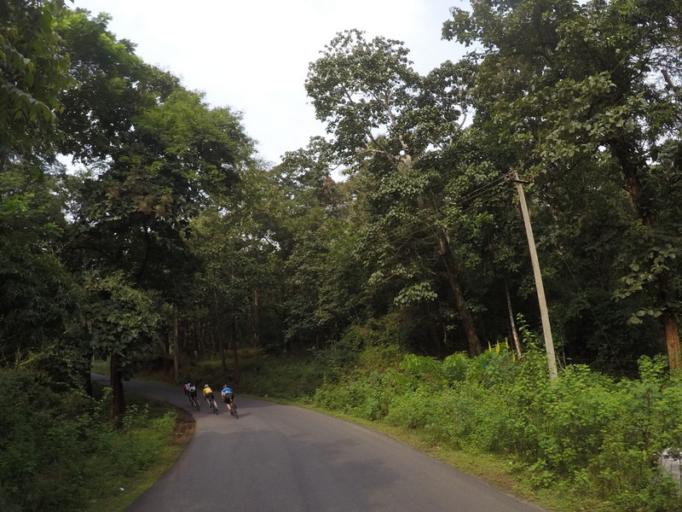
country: IN
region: Karnataka
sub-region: Chikmagalur
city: Koppa
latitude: 13.3522
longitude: 75.4871
